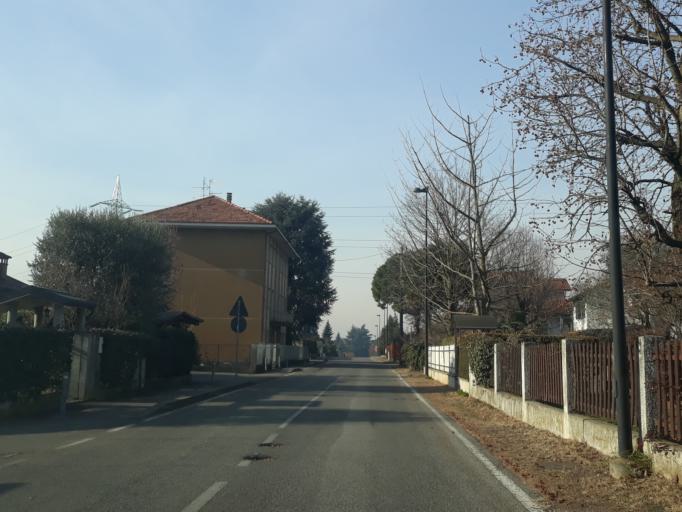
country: IT
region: Lombardy
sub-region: Provincia di Monza e Brianza
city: Bellusco
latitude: 45.6225
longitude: 9.4130
